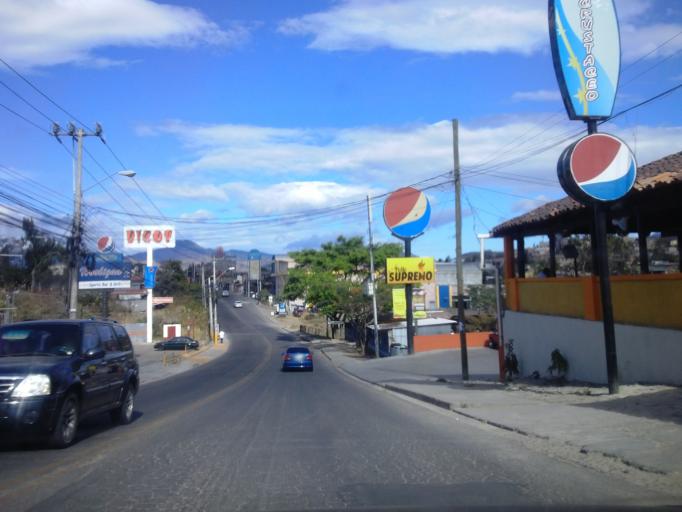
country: HN
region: Francisco Morazan
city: Tegucigalpa
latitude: 14.0532
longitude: -87.2259
